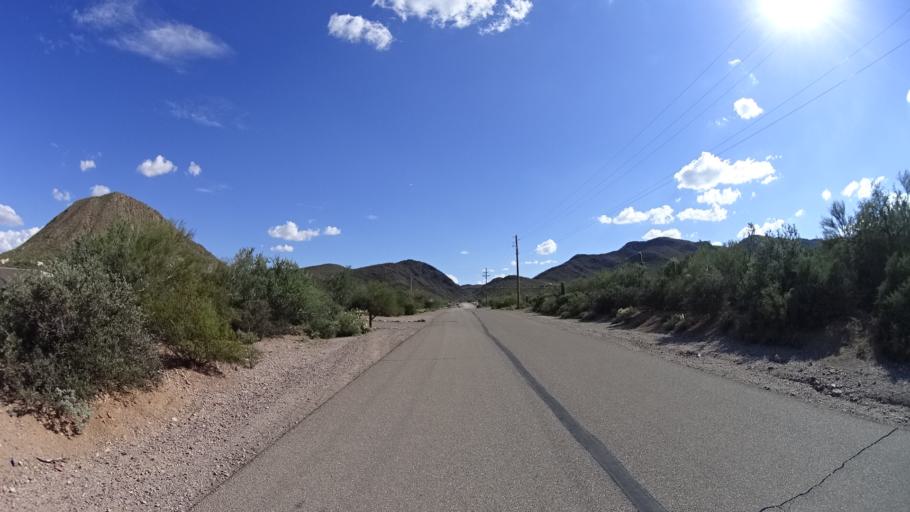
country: US
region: Arizona
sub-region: Pima County
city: Tucson Estates
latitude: 32.2326
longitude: -111.0627
